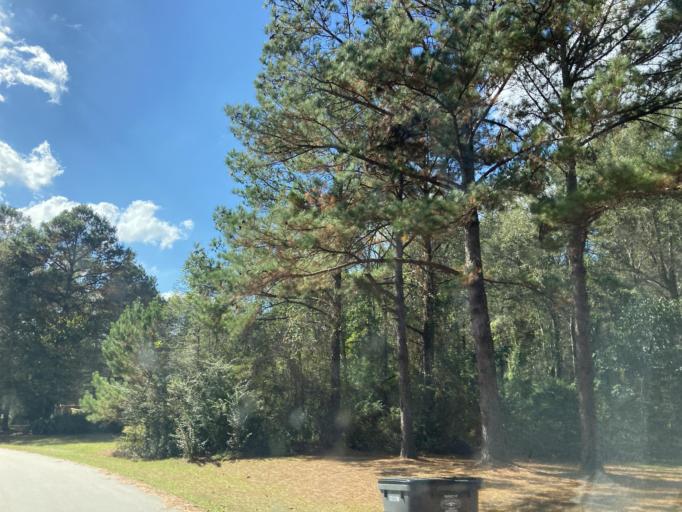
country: US
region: Mississippi
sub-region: Lamar County
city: Sumrall
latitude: 31.3644
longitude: -89.5166
